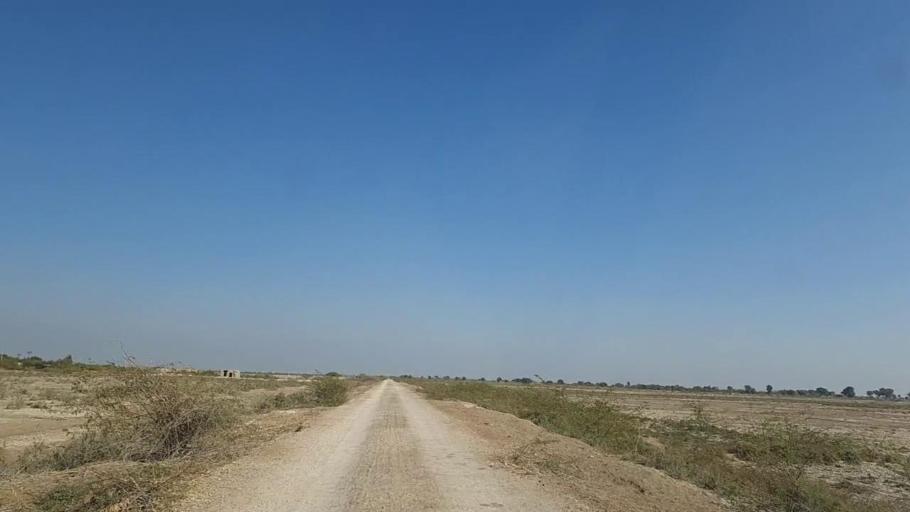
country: PK
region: Sindh
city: Samaro
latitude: 25.3990
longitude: 69.4206
